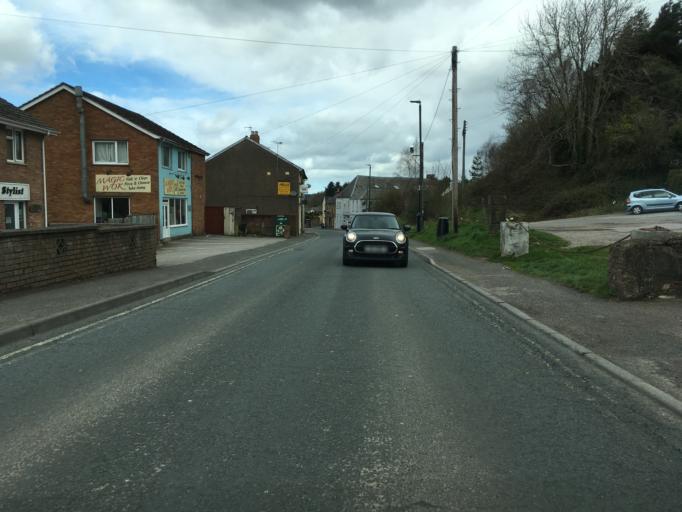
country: GB
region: England
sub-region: Gloucestershire
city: Cinderford
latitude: 51.8278
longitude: -2.5014
